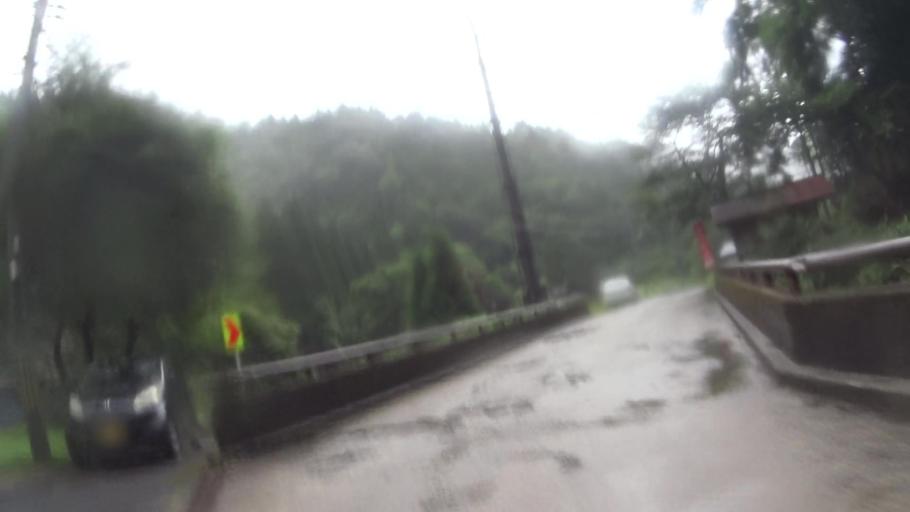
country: JP
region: Shiga Prefecture
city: Kitahama
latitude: 35.2604
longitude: 135.7690
